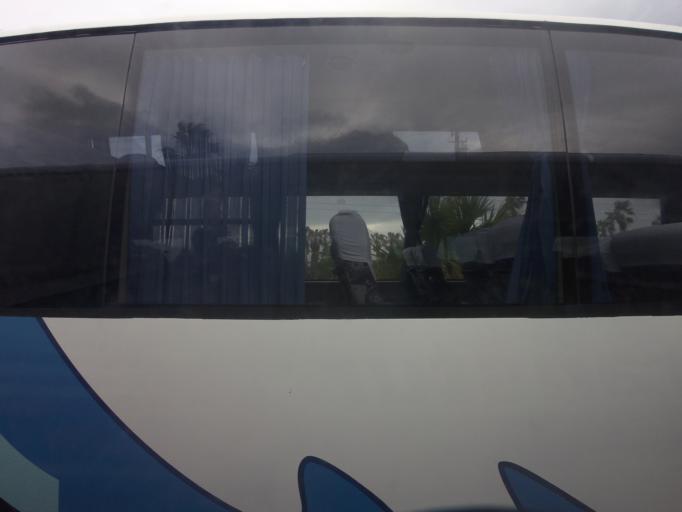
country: CU
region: Matanzas
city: Varadero
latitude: 23.1376
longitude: -81.2769
